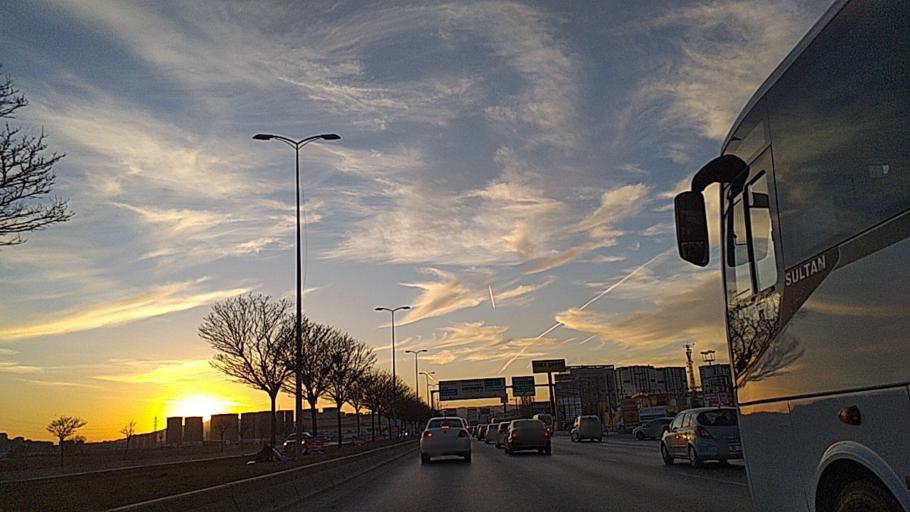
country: TR
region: Ankara
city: Etimesgut
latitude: 39.9644
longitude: 32.6430
